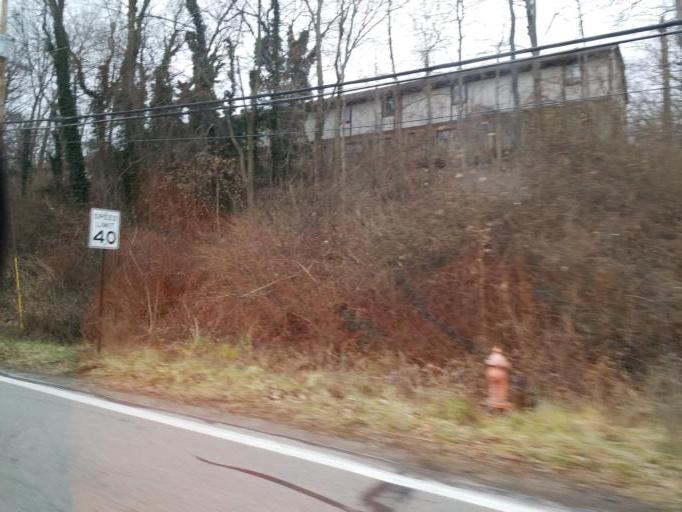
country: US
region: Ohio
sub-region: Franklin County
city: Huber Ridge
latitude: 40.0948
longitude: -82.9352
